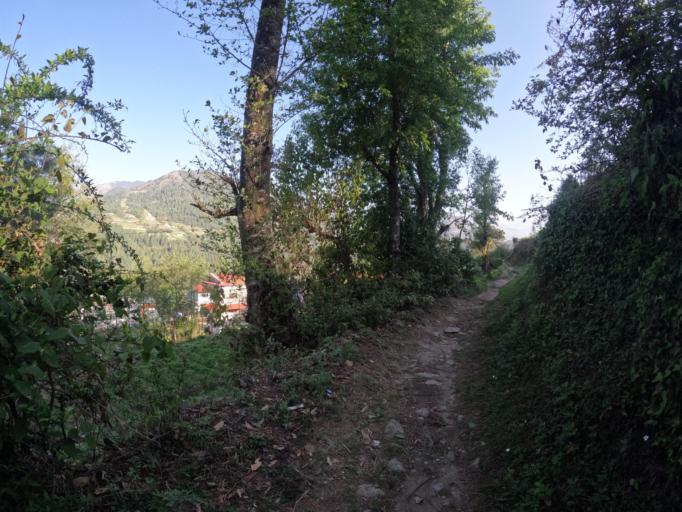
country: NP
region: Eastern Region
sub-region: Sagarmatha Zone
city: Namche Bazar
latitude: 27.4907
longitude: 86.5819
